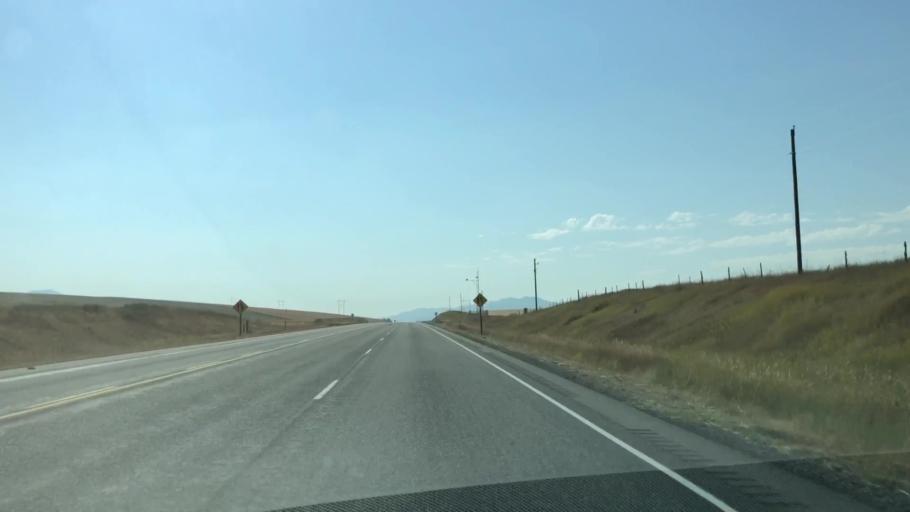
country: US
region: Idaho
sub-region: Teton County
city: Victor
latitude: 43.5283
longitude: -111.5015
